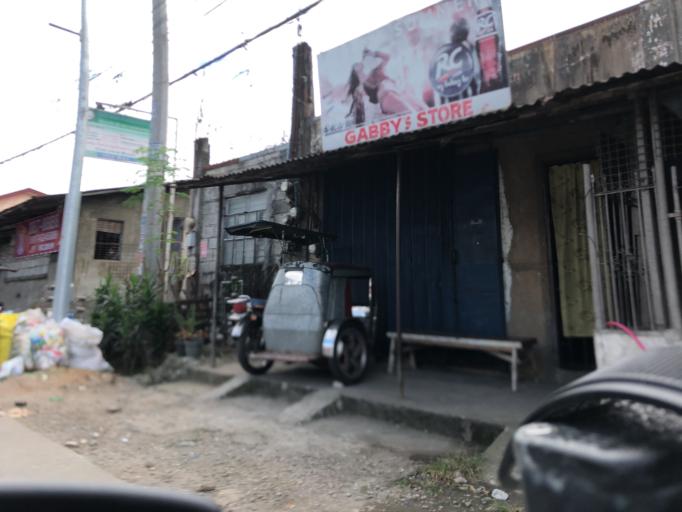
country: PH
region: Central Luzon
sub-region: Province of Bulacan
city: San Jose del Monte
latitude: 14.7443
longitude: 121.0584
